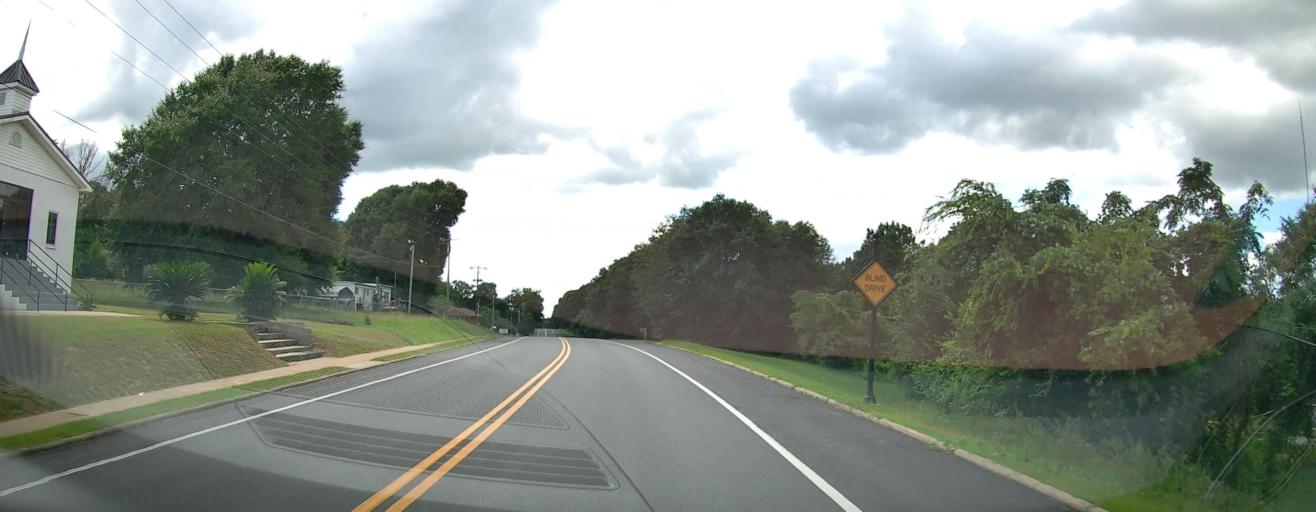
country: US
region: Georgia
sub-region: Chattahoochee County
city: Cusseta
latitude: 32.3081
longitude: -84.7837
